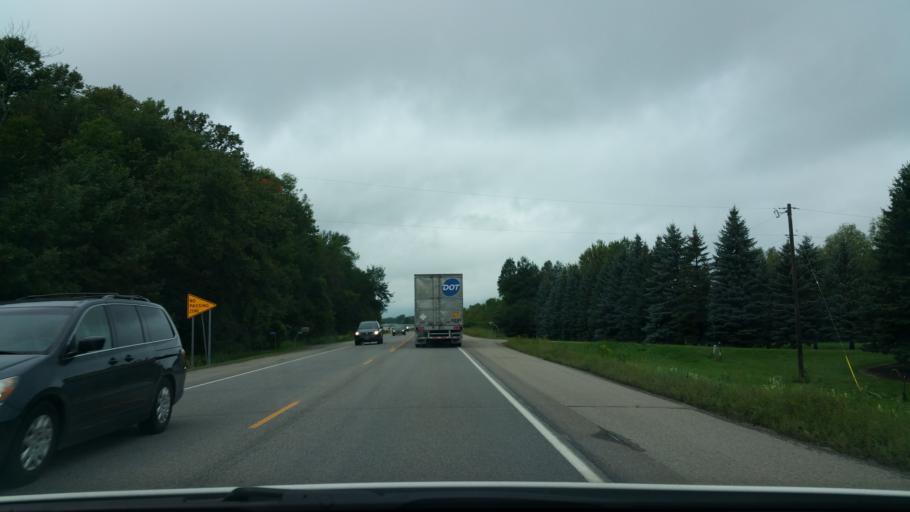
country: US
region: Minnesota
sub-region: Rice County
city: Dundas
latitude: 44.4720
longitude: -93.2793
